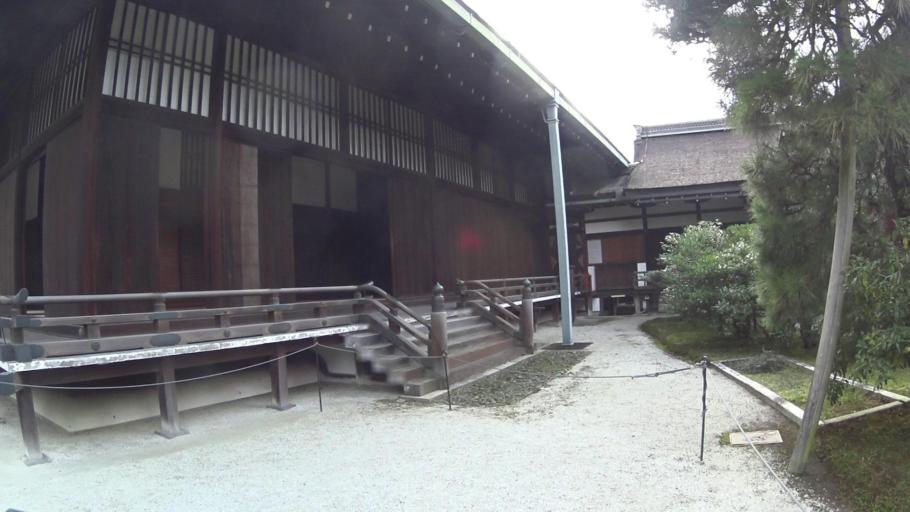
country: JP
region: Kyoto
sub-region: Kyoto-shi
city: Kamigyo-ku
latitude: 35.0254
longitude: 135.7630
